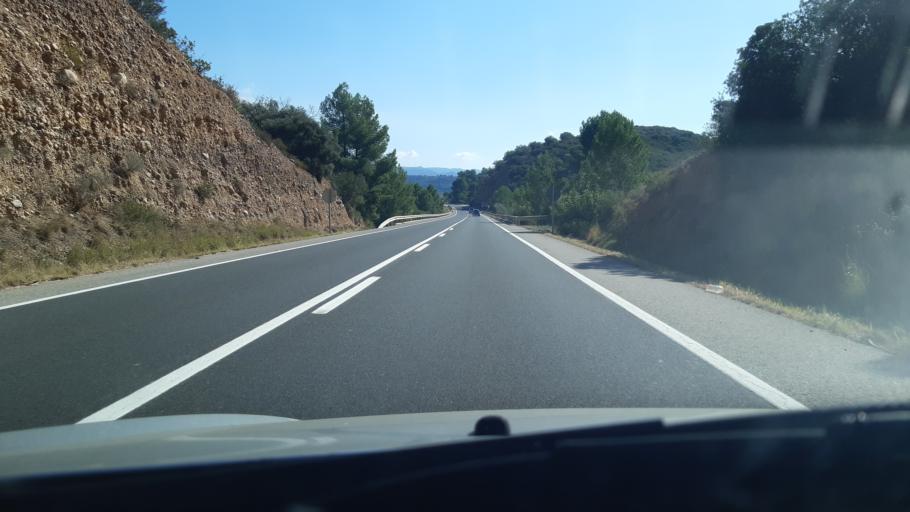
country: ES
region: Catalonia
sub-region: Provincia de Tarragona
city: Tivenys
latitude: 40.9250
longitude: 0.4877
